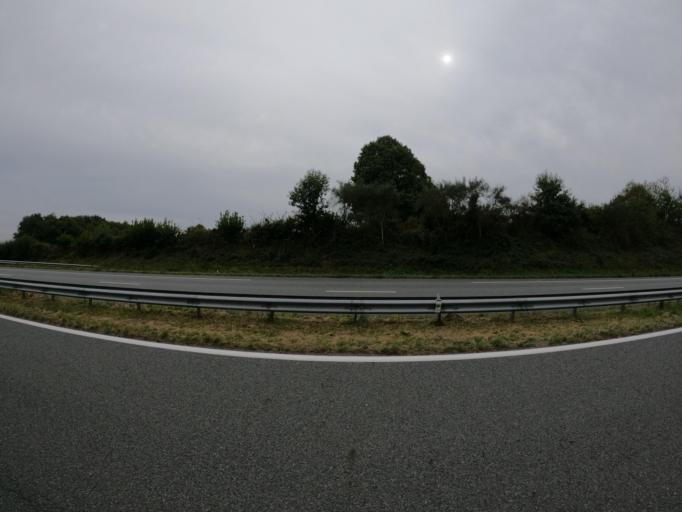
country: FR
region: Limousin
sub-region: Departement de la Creuse
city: Le Grand-Bourg
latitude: 46.2141
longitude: 1.6368
